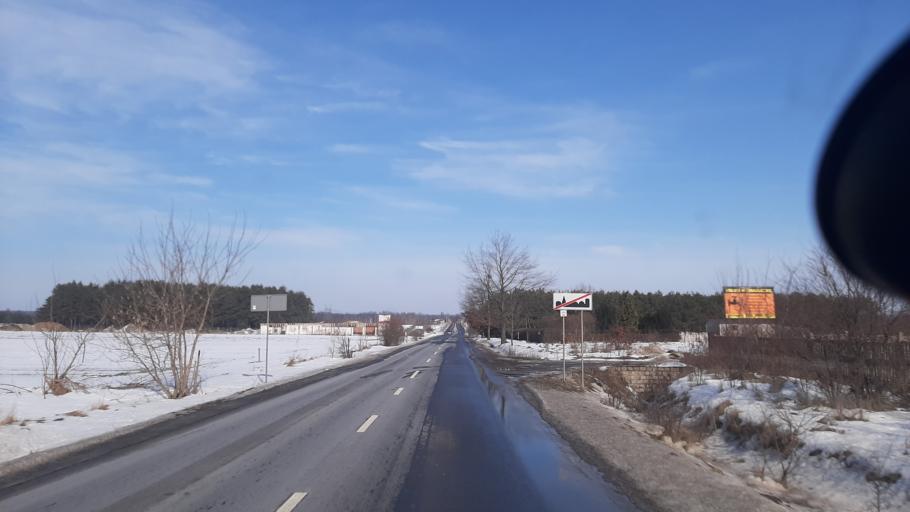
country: PL
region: Lublin Voivodeship
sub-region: Powiat pulawski
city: Kurow
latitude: 51.3999
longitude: 22.2001
